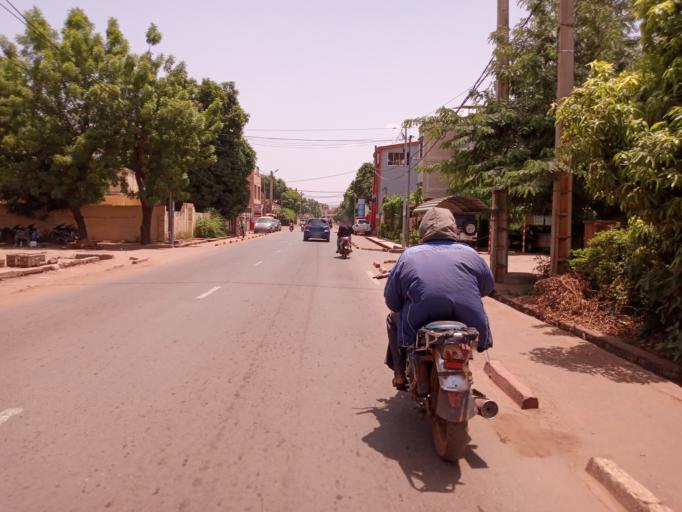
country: ML
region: Bamako
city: Bamako
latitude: 12.6448
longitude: -7.9772
